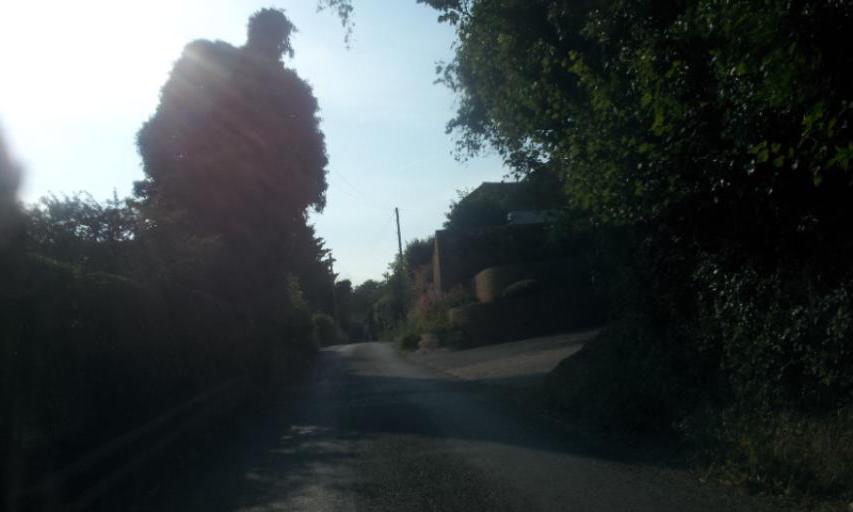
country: GB
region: England
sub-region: Kent
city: Boxley
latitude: 51.2955
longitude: 0.5723
